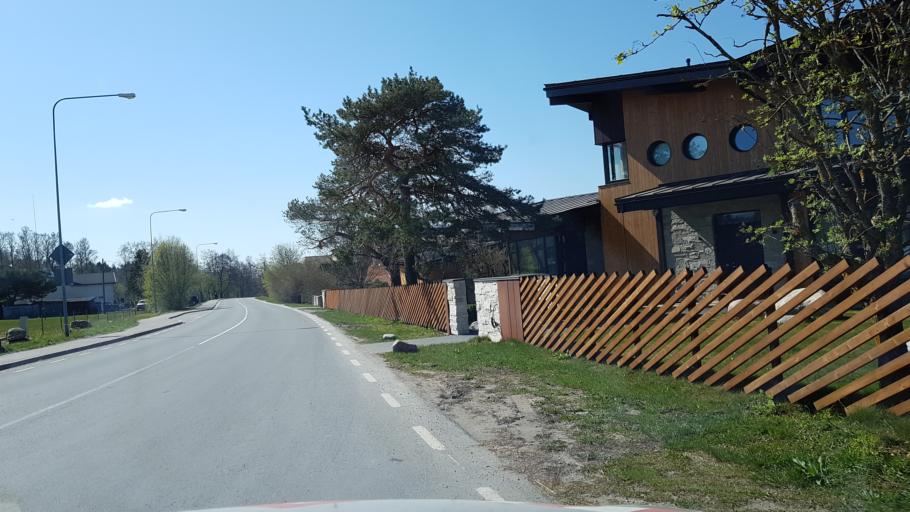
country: EE
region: Harju
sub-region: Viimsi vald
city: Rummu
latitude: 59.5619
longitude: 24.8007
